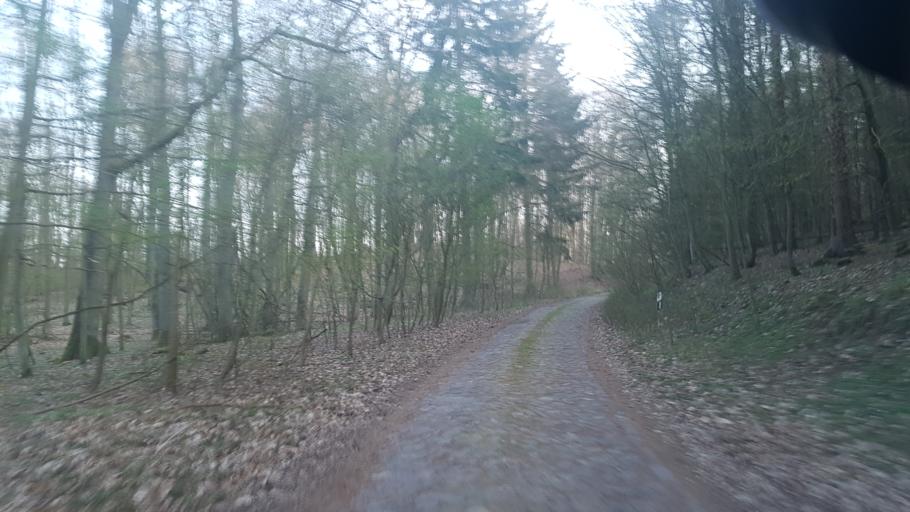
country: DE
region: Brandenburg
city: Gramzow
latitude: 53.2033
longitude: 13.9360
